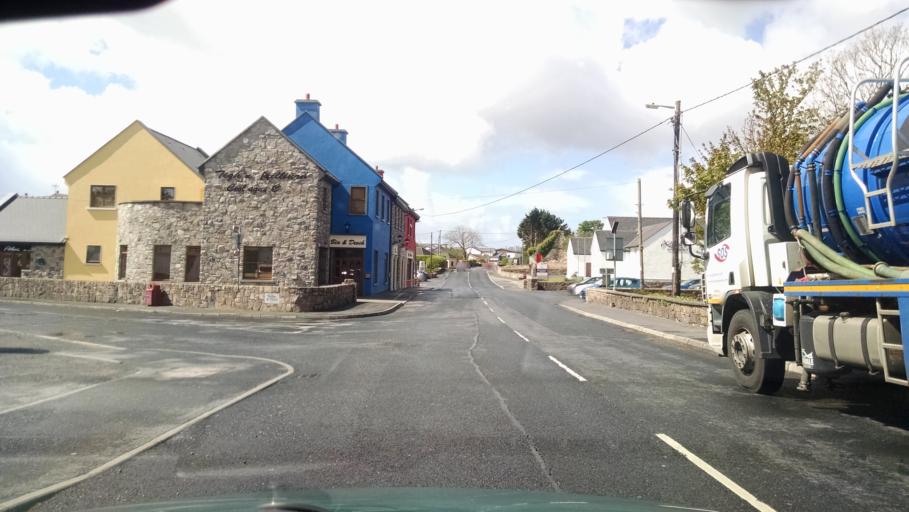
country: IE
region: Connaught
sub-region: County Galway
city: Oughterard
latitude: 53.2645
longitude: -9.5975
